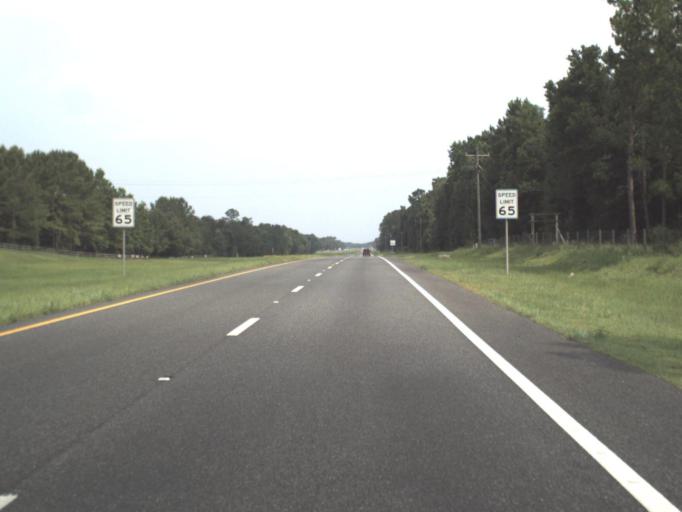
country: US
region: Florida
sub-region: Levy County
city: Williston
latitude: 29.3635
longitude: -82.4072
